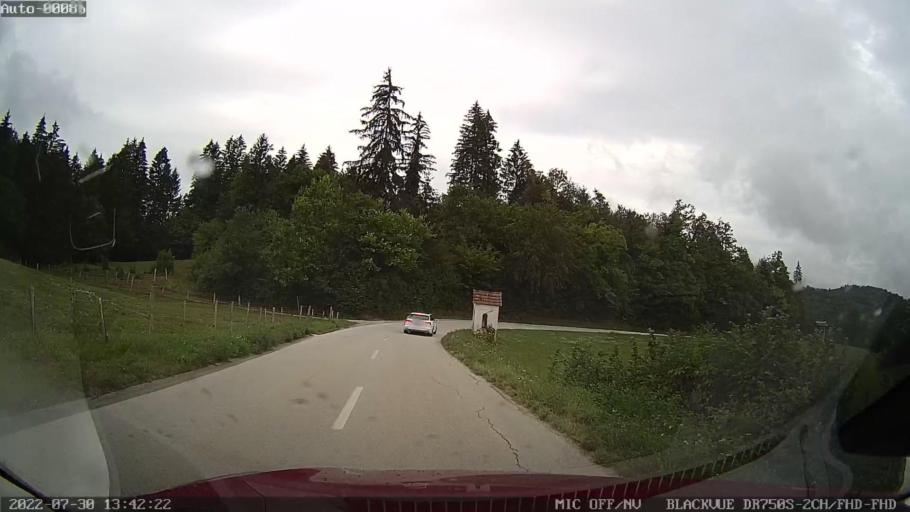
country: SI
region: Ivancna Gorica
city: Sentvid pri Sticni
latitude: 45.9060
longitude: 14.8956
